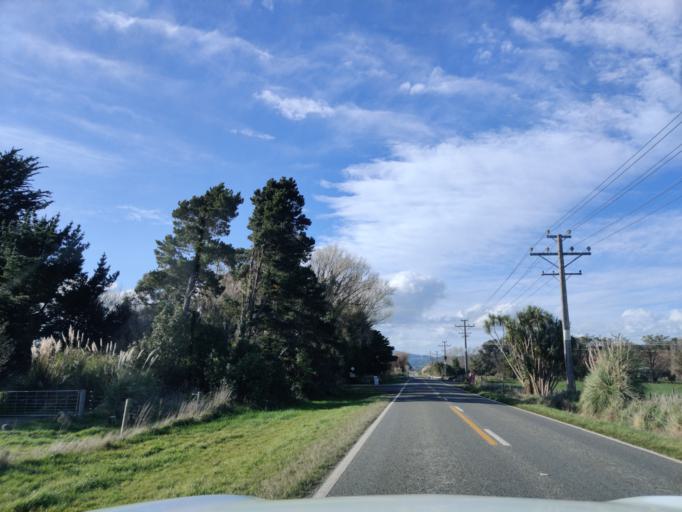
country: NZ
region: Manawatu-Wanganui
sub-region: Palmerston North City
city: Palmerston North
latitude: -40.3450
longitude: 175.7092
